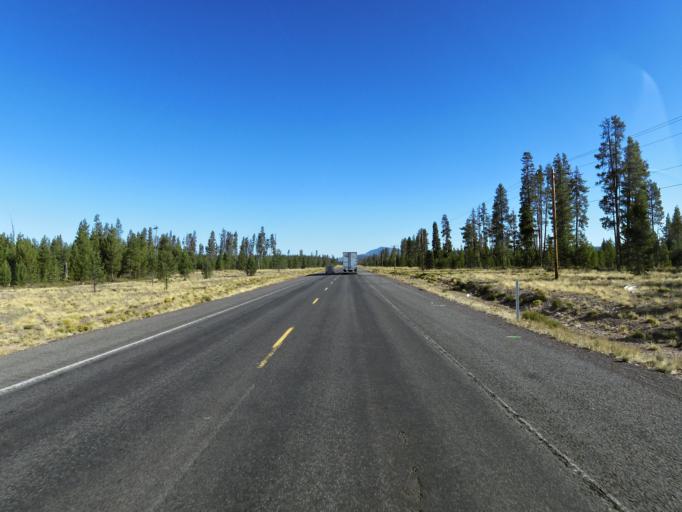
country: US
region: Oregon
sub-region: Deschutes County
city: La Pine
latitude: 43.1577
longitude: -121.7932
